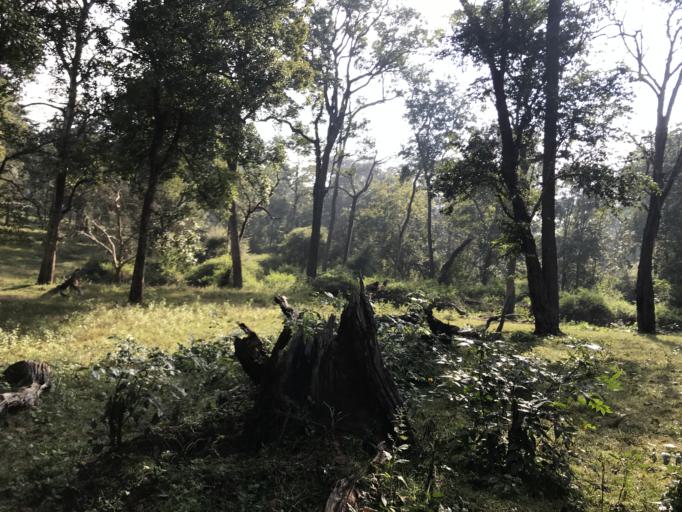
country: IN
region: Karnataka
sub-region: Mysore
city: Heggadadevankote
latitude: 11.9513
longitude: 76.2183
